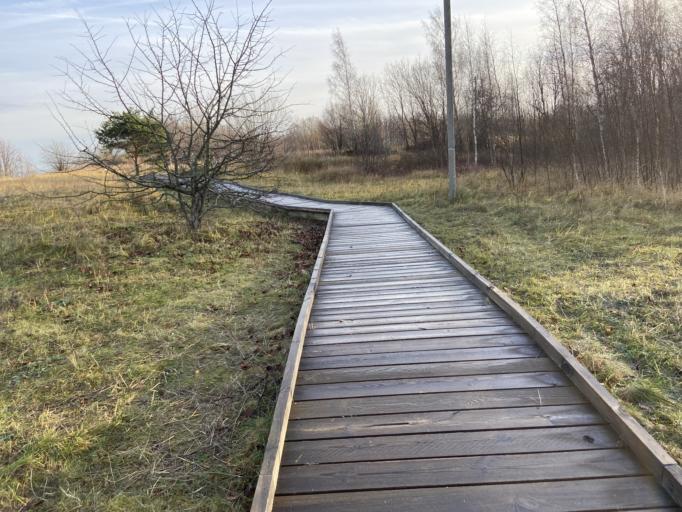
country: EE
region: Harju
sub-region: Tallinna linn
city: Tallinn
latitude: 59.4770
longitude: 24.7135
